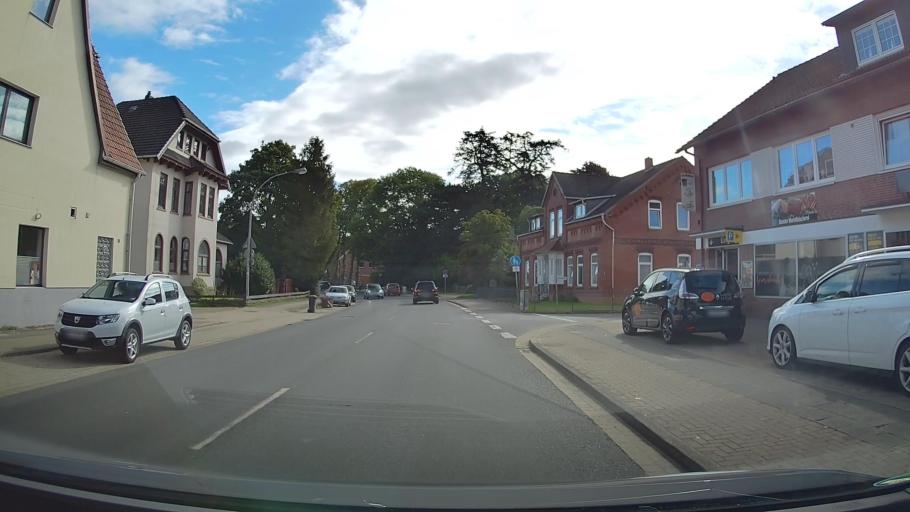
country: DE
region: Lower Saxony
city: Loxstedt
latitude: 53.4481
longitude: 8.6035
